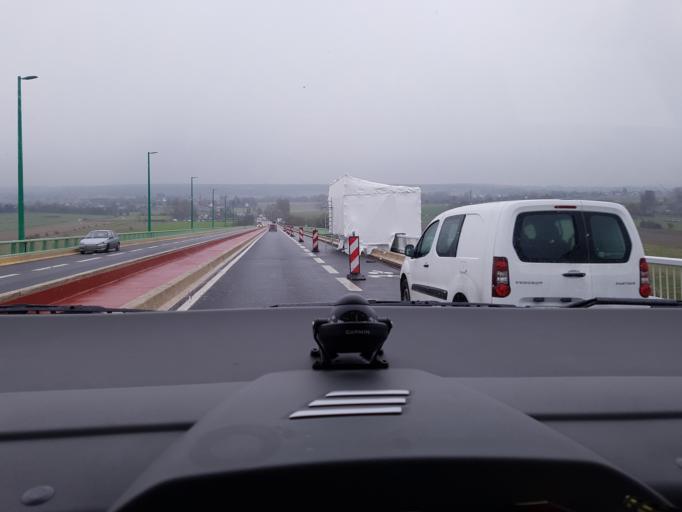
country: FR
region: Haute-Normandie
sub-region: Departement de la Seine-Maritime
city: Caudebec-en-Caux
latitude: 49.5170
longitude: 0.7445
